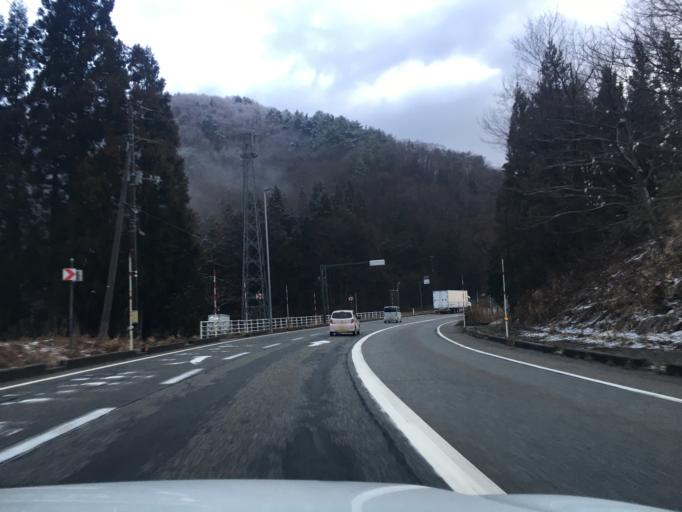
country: JP
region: Niigata
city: Murakami
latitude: 38.4219
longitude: 139.5678
